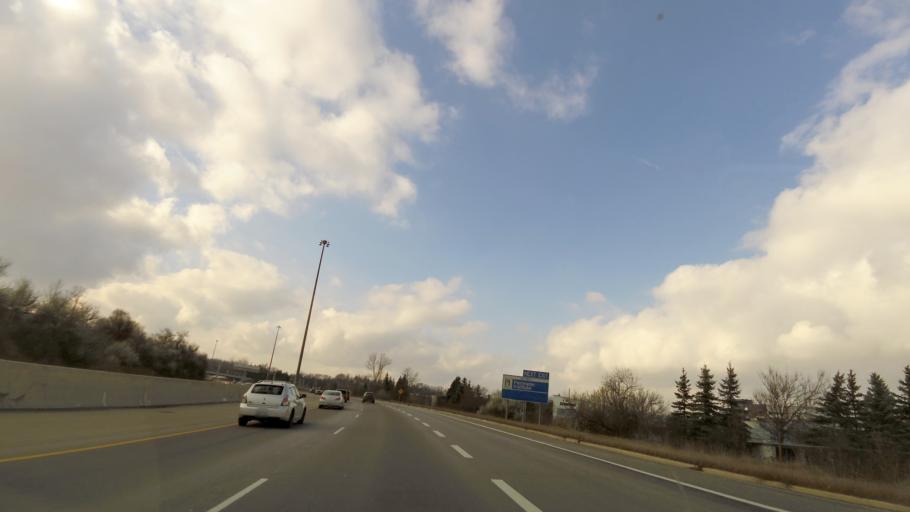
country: CA
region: Ontario
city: Waterloo
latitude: 43.4738
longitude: -80.4787
